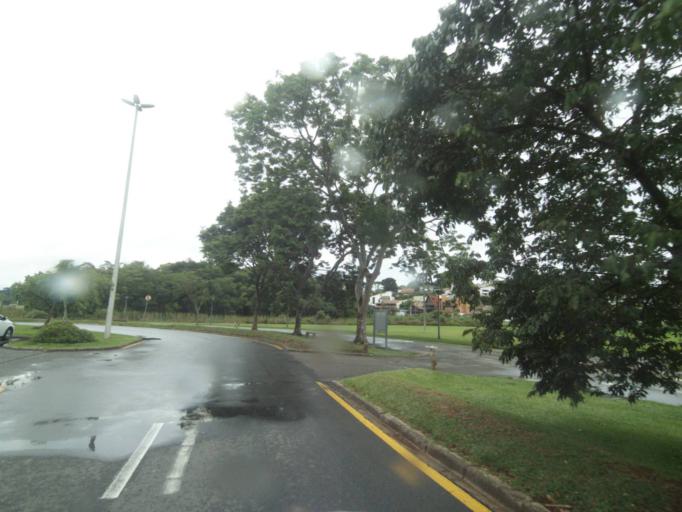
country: BR
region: Parana
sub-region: Curitiba
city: Curitiba
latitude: -25.4264
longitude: -49.3083
